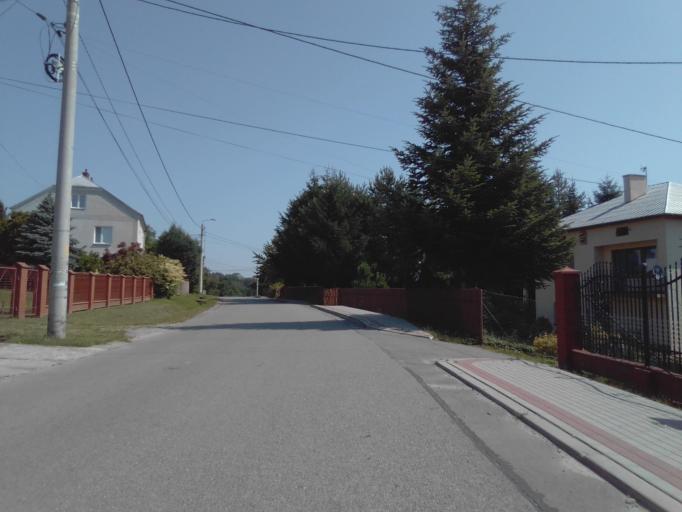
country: PL
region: Subcarpathian Voivodeship
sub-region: Powiat ropczycko-sedziszowski
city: Ropczyce
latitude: 50.0251
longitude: 21.6361
